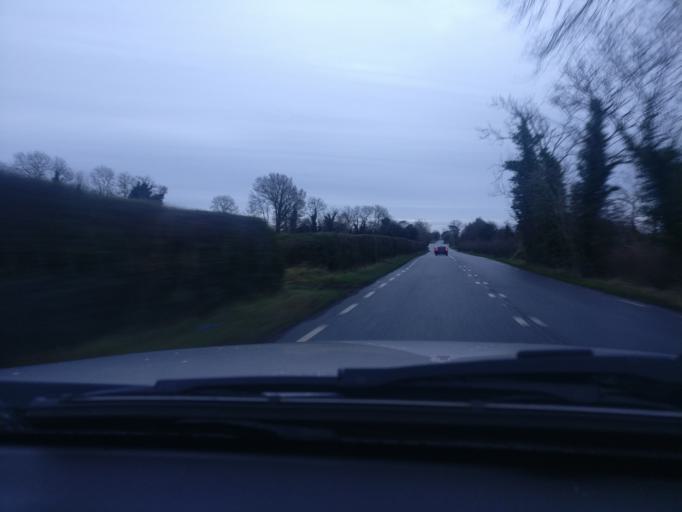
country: IE
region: Leinster
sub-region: An Mhi
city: Navan
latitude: 53.6889
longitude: -6.7736
